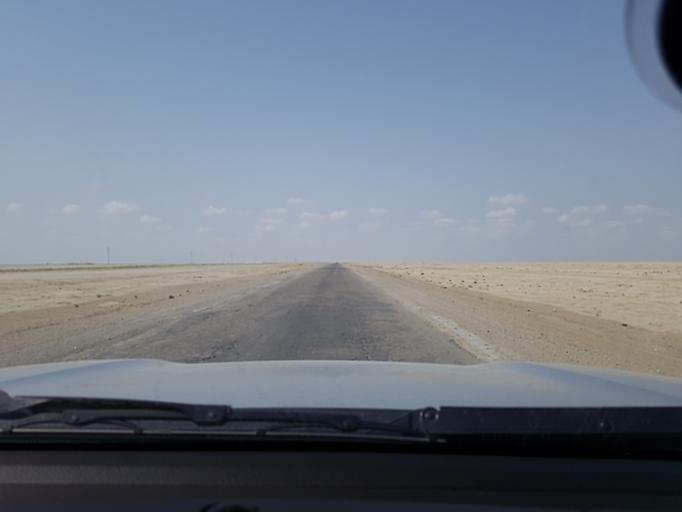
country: TM
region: Balkan
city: Gumdag
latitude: 38.6479
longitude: 54.3824
